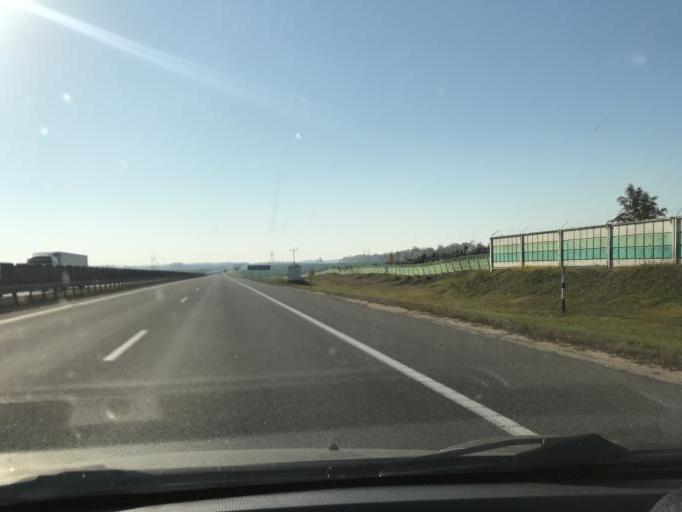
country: BY
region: Minsk
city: Pryvol'ny
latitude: 53.8136
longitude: 27.8132
